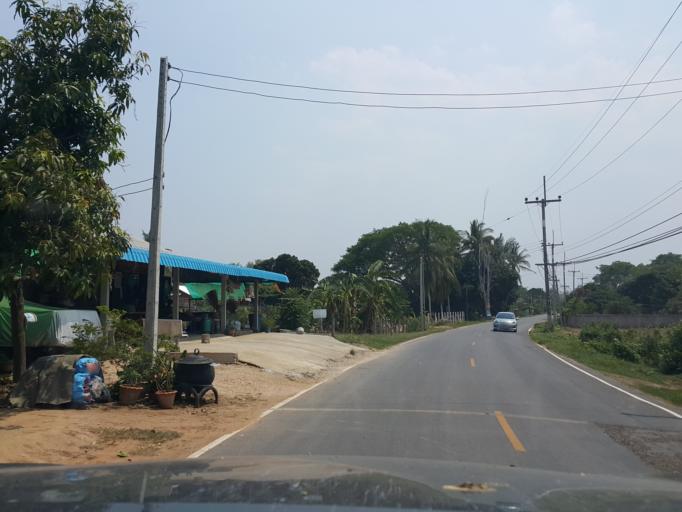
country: TH
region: Lampang
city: Mae Phrik
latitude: 17.5067
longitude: 99.1323
